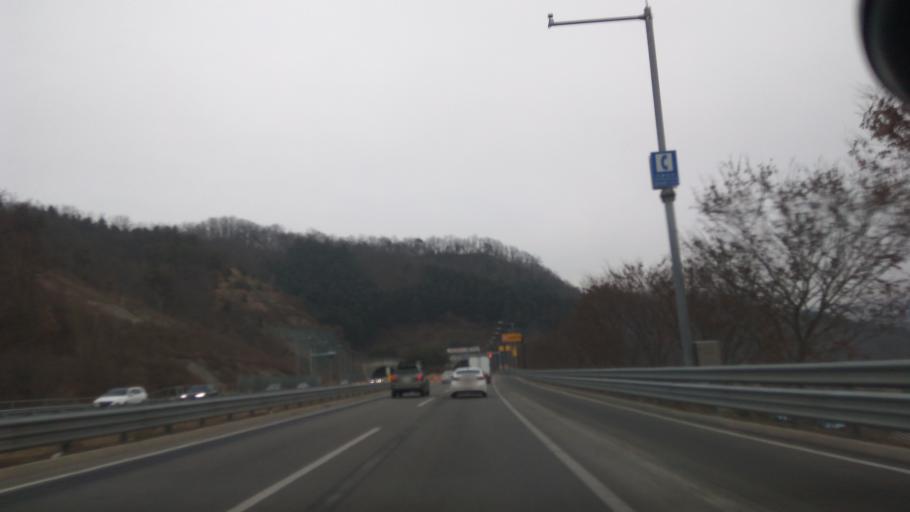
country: KR
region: Gangwon-do
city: Sindong
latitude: 37.7424
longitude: 127.6796
